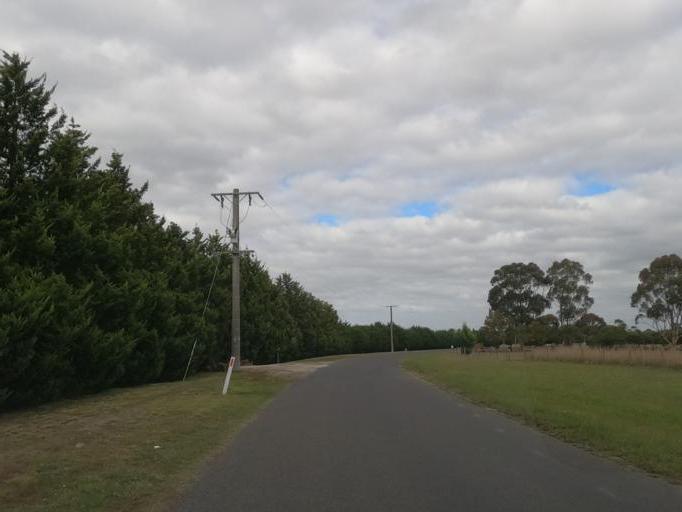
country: AU
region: Victoria
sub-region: Hume
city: Greenvale
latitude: -37.5524
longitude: 144.8695
